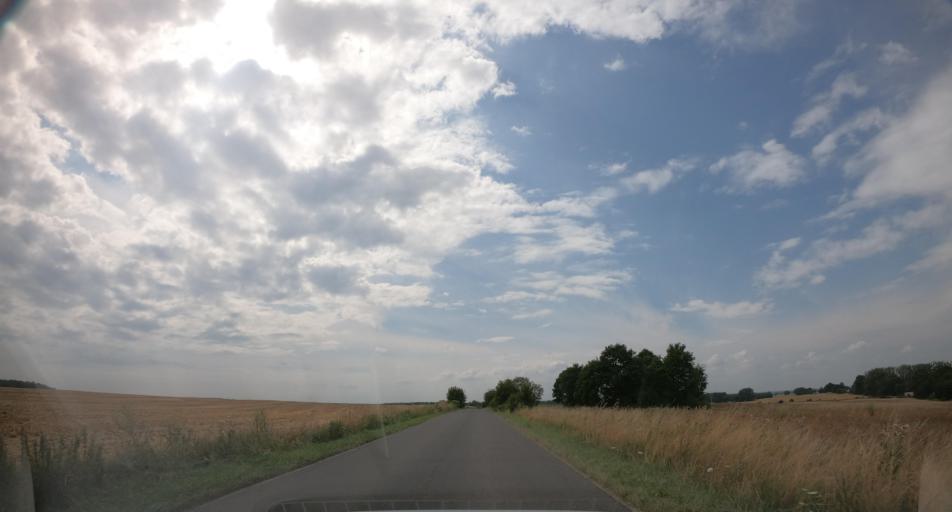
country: PL
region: West Pomeranian Voivodeship
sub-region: Powiat walecki
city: Tuczno
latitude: 53.2188
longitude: 16.1984
